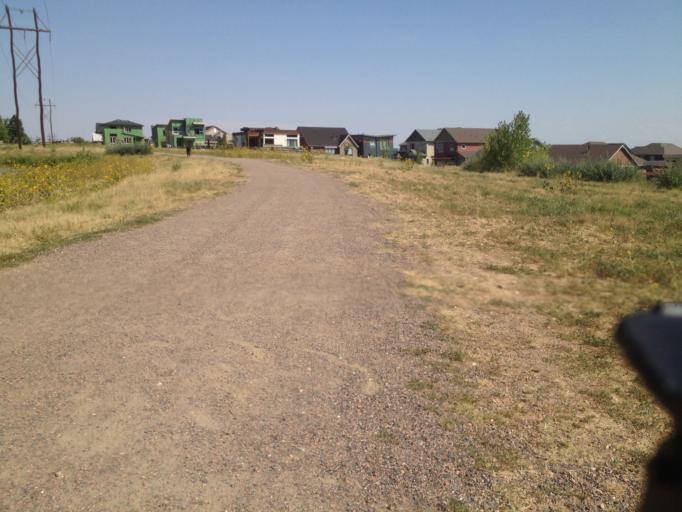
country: US
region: Colorado
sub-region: Boulder County
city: Louisville
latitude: 39.9906
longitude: -105.1222
